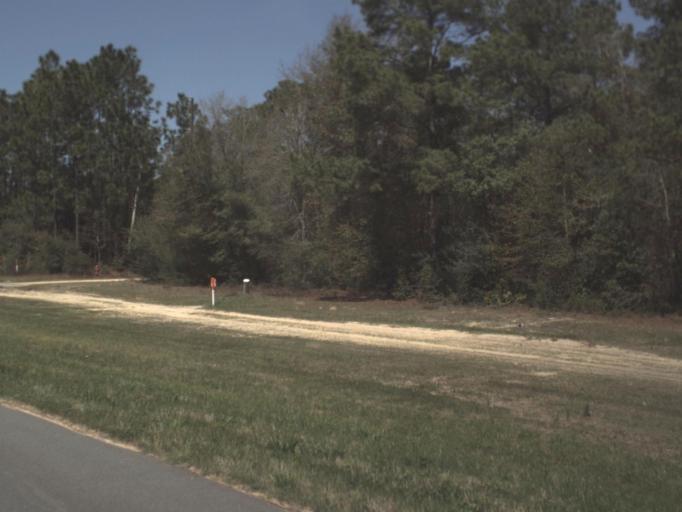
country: US
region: Florida
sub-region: Walton County
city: DeFuniak Springs
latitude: 30.7511
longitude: -86.2745
